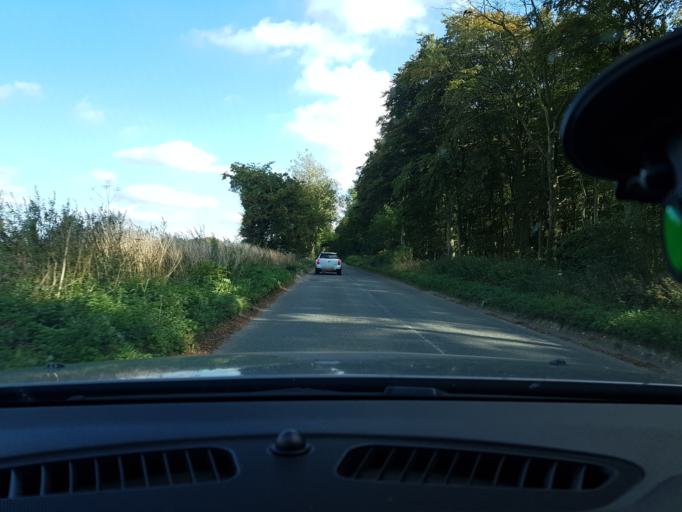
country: GB
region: England
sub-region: Wiltshire
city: Aldbourne
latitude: 51.5106
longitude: -1.6262
